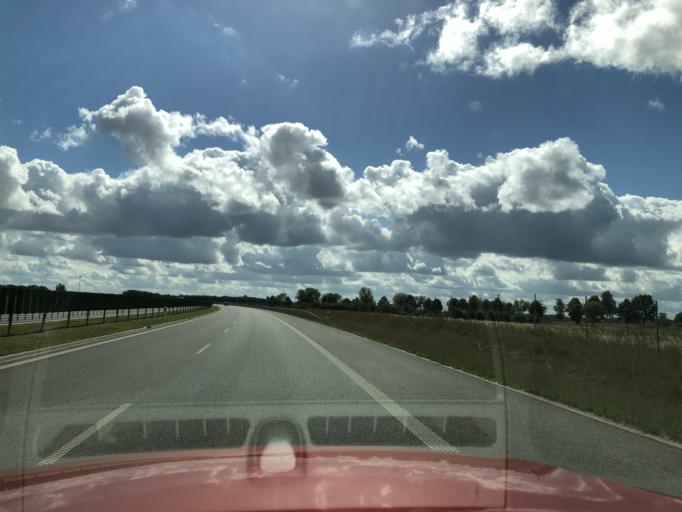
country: PL
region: West Pomeranian Voivodeship
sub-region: Powiat szczecinecki
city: Szczecinek
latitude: 53.6593
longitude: 16.7381
